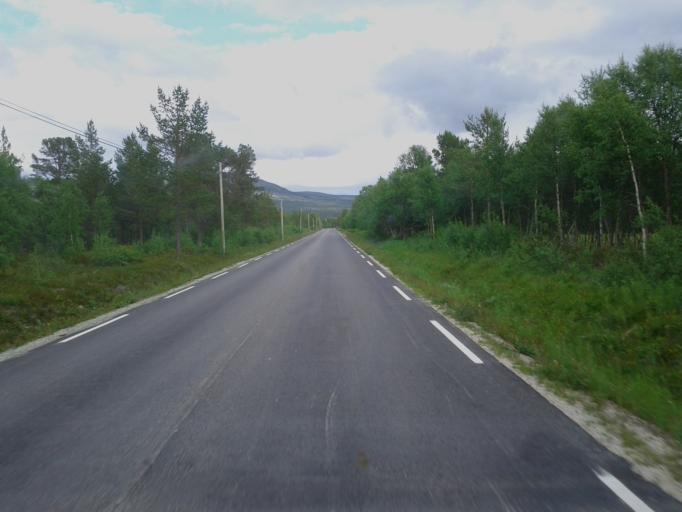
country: NO
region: Sor-Trondelag
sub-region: Roros
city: Roros
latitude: 62.3053
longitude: 11.7046
